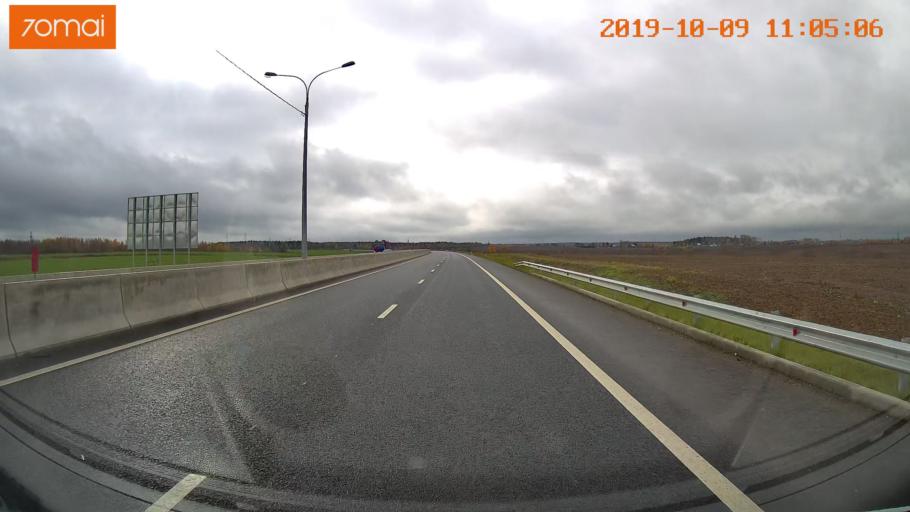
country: RU
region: Vologda
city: Molochnoye
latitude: 59.2042
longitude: 39.7600
